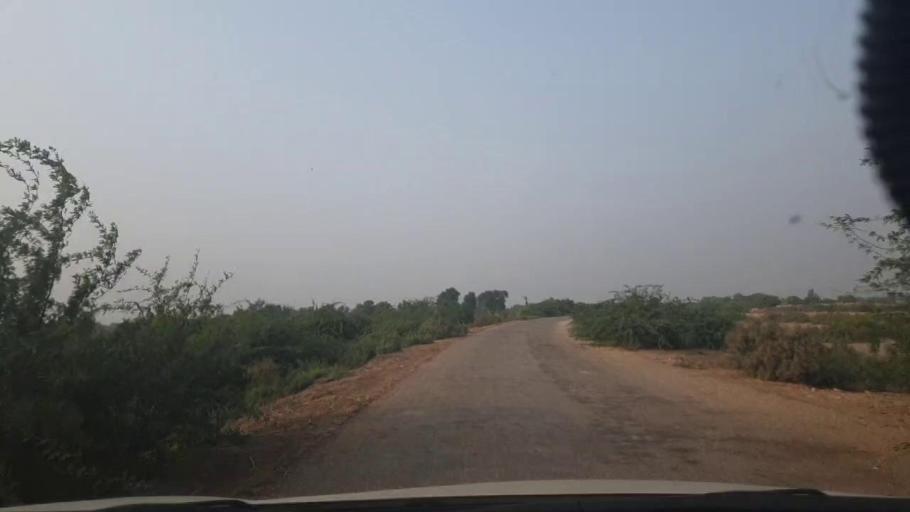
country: PK
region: Sindh
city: Bulri
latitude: 24.8223
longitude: 68.4034
